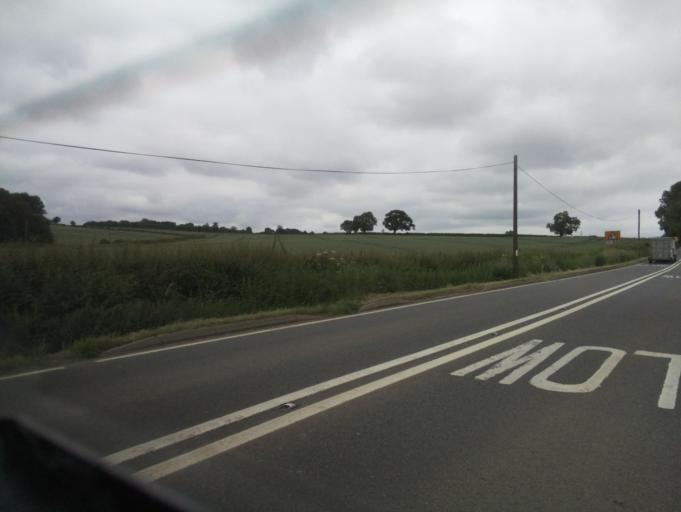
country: GB
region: England
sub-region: Leicestershire
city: Grimston
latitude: 52.7715
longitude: -0.9844
